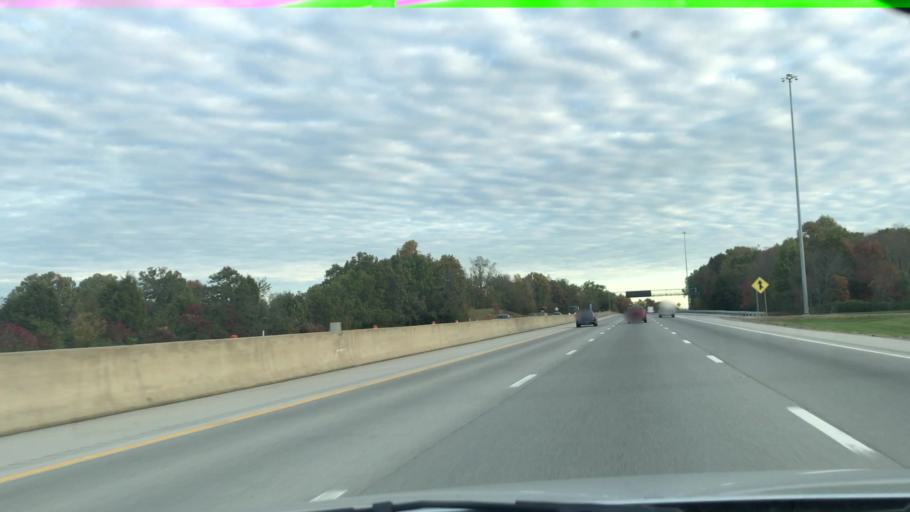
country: US
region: Kentucky
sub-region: Simpson County
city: Franklin
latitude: 36.6456
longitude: -86.5691
